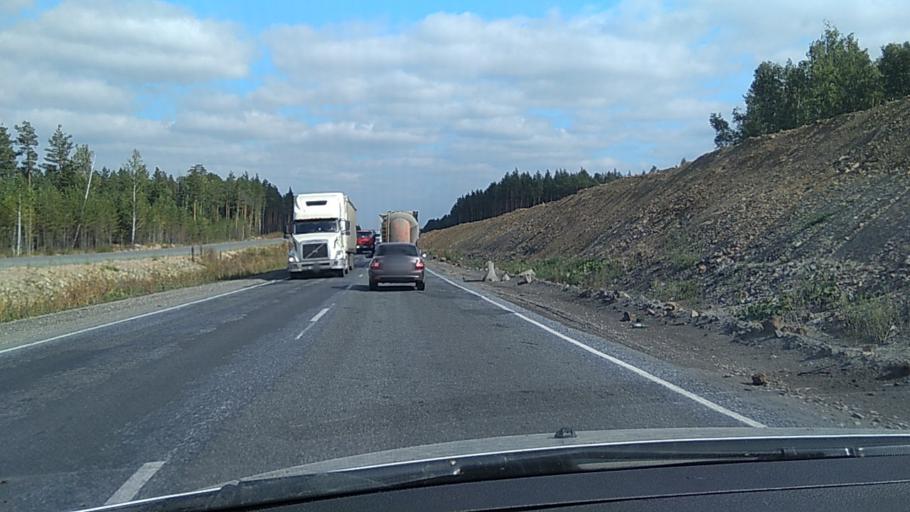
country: RU
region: Chelyabinsk
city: Chebarkul'
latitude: 54.9234
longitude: 60.2564
